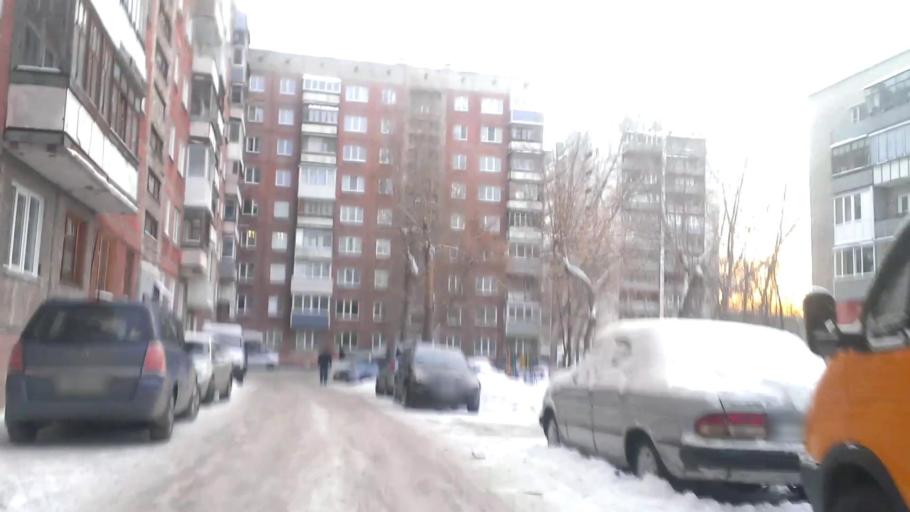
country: RU
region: Altai Krai
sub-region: Gorod Barnaulskiy
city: Barnaul
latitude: 53.3466
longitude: 83.6951
